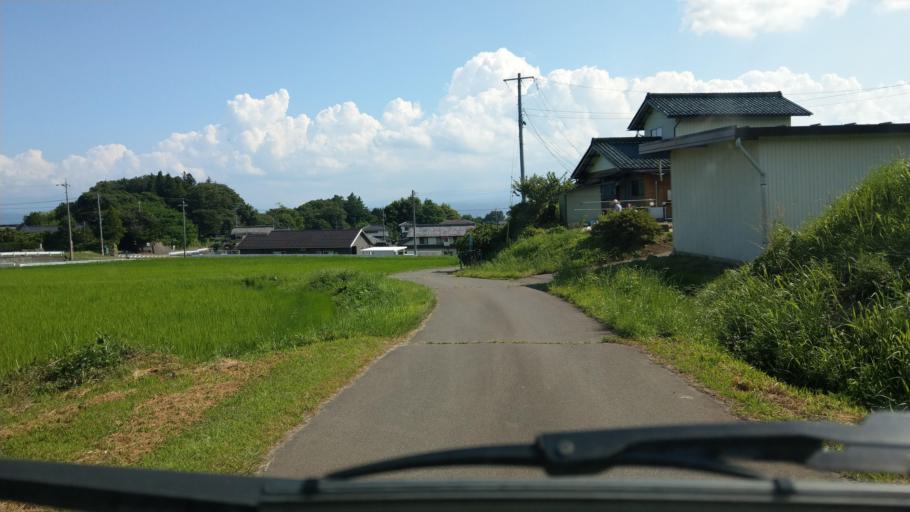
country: JP
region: Nagano
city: Komoro
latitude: 36.3238
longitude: 138.4497
